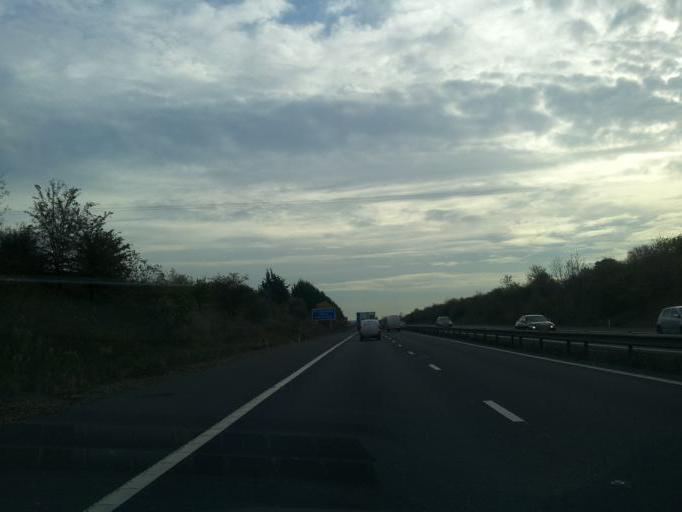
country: GB
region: England
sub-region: Cambridgeshire
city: Duxford
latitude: 52.1154
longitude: 0.1276
